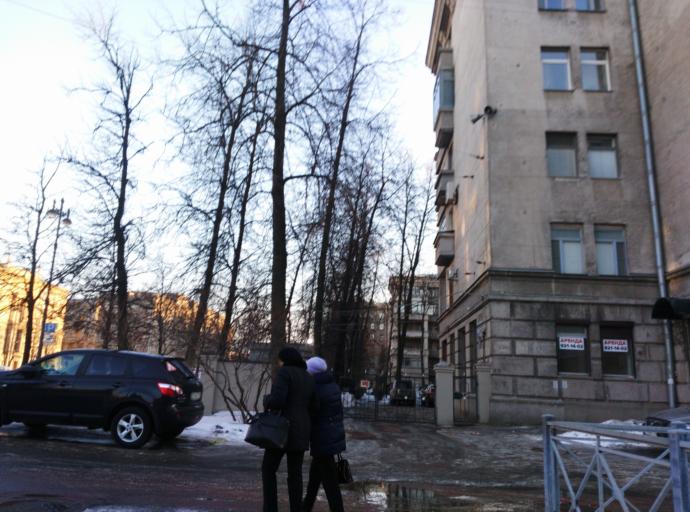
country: RU
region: St.-Petersburg
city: Kupchino
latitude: 59.8744
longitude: 30.3194
